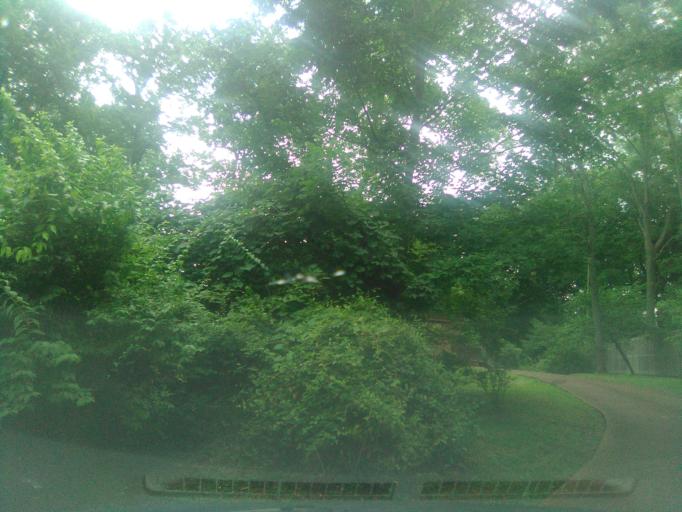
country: US
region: Tennessee
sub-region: Davidson County
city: Belle Meade
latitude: 36.0892
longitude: -86.8741
